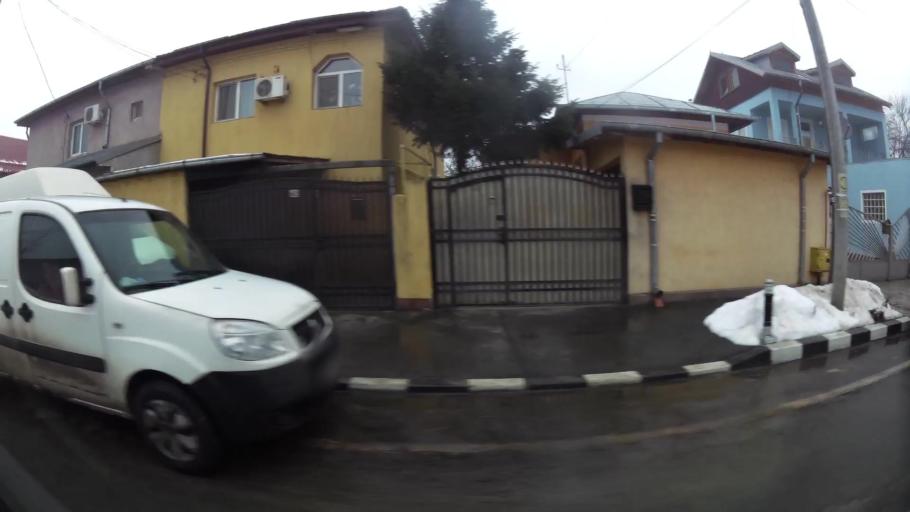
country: RO
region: Ilfov
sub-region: Comuna Chiajna
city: Chiajna
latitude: 44.4596
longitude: 25.9706
